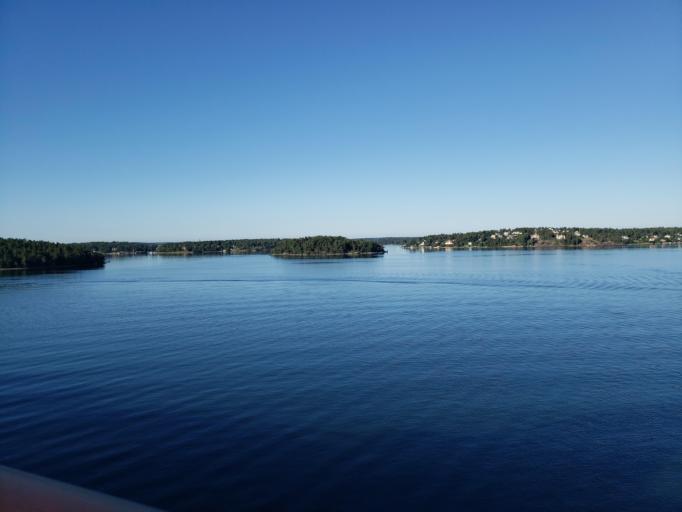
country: SE
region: Stockholm
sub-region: Vaxholms Kommun
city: Vaxholm
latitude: 59.4336
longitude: 18.3833
